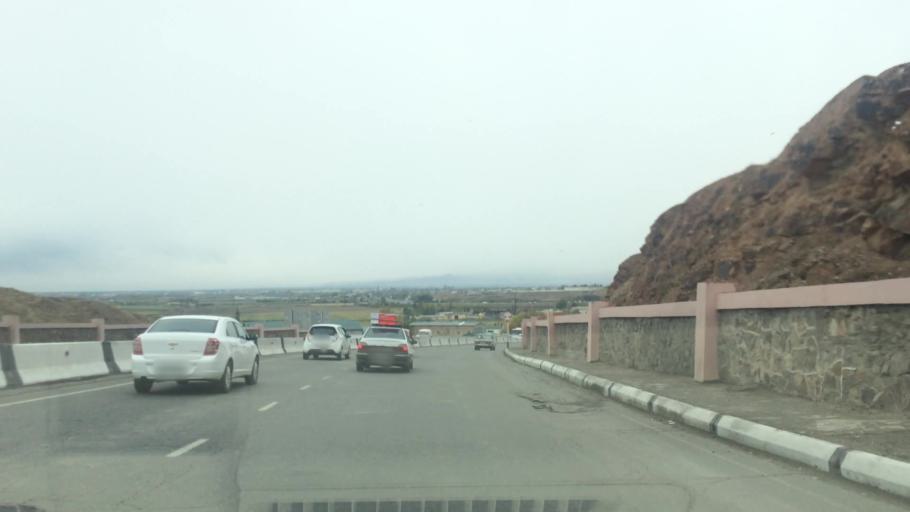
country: UZ
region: Samarqand
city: Jomboy
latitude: 39.6845
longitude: 67.0516
